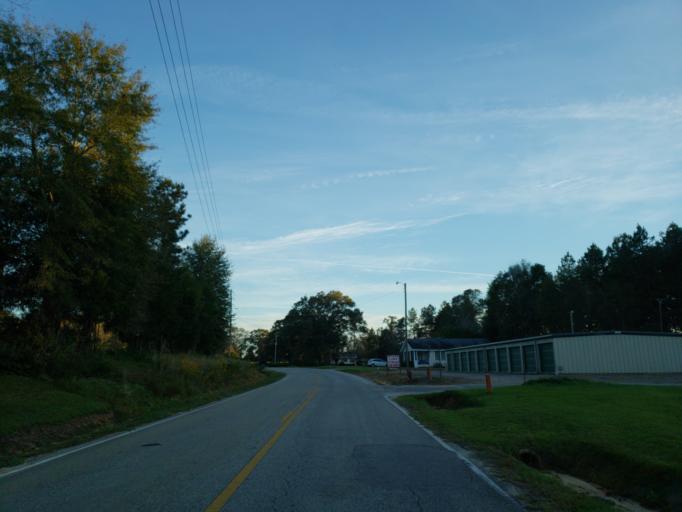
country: US
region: Mississippi
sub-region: Wayne County
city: Belmont
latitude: 31.4289
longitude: -88.4726
